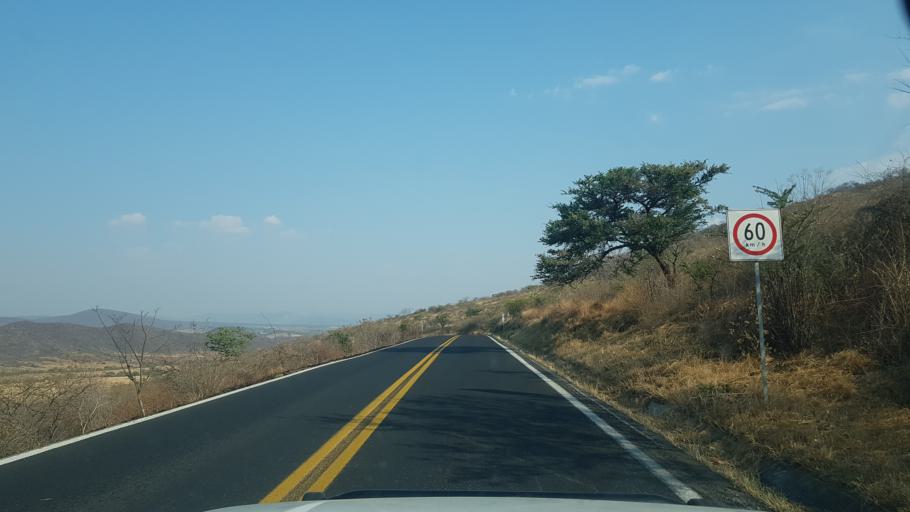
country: MX
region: Puebla
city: Calmeca
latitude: 18.6455
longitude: -98.5985
